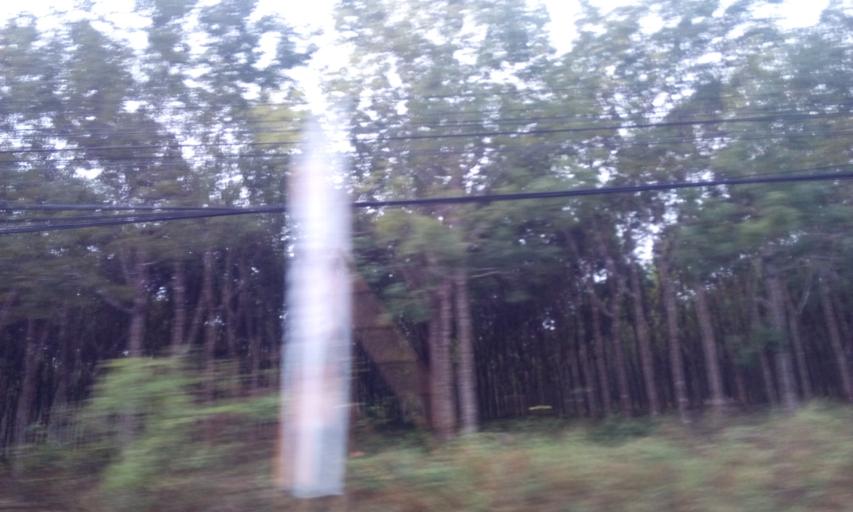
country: TH
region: Trat
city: Khao Saming
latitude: 12.3731
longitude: 102.3854
